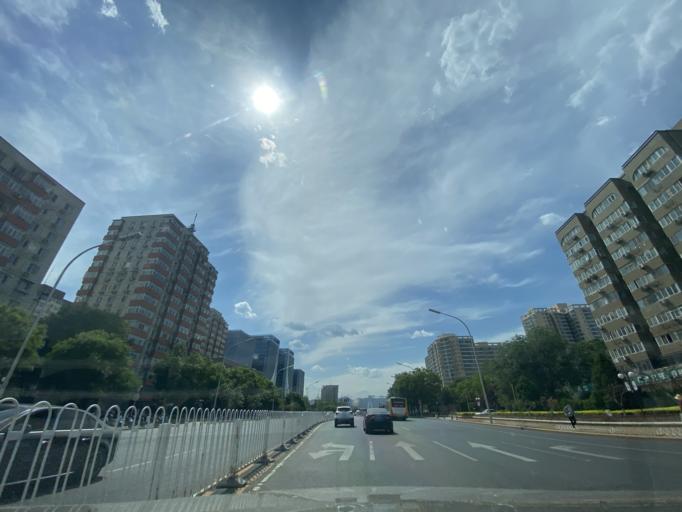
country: CN
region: Beijing
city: Lugu
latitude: 39.9061
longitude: 116.1826
